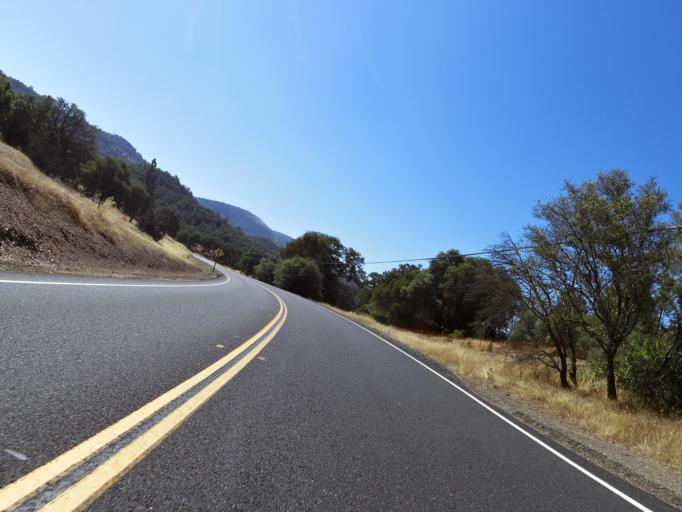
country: US
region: California
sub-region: Tuolumne County
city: Tuolumne City
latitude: 37.7086
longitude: -120.2027
